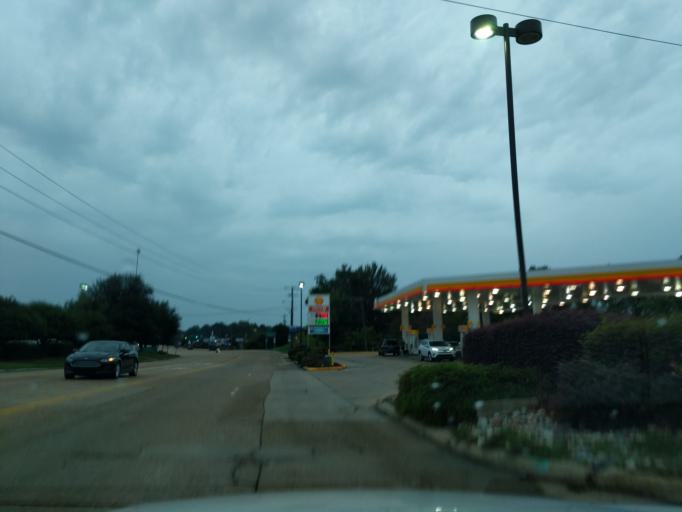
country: US
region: Mississippi
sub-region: Warren County
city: Vicksburg
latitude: 32.3141
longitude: -90.8989
